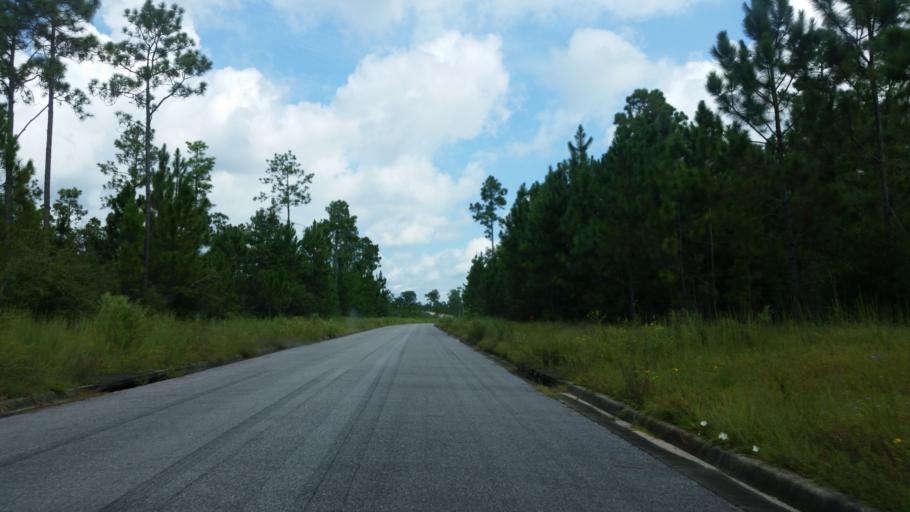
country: US
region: Florida
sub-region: Escambia County
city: Cantonment
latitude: 30.6429
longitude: -87.3503
